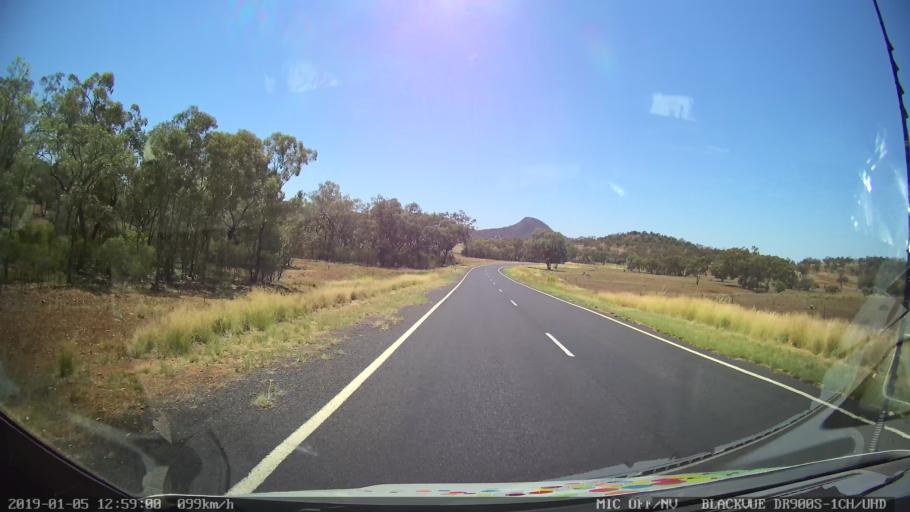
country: AU
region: New South Wales
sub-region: Narrabri
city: Boggabri
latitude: -31.1126
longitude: 149.7589
